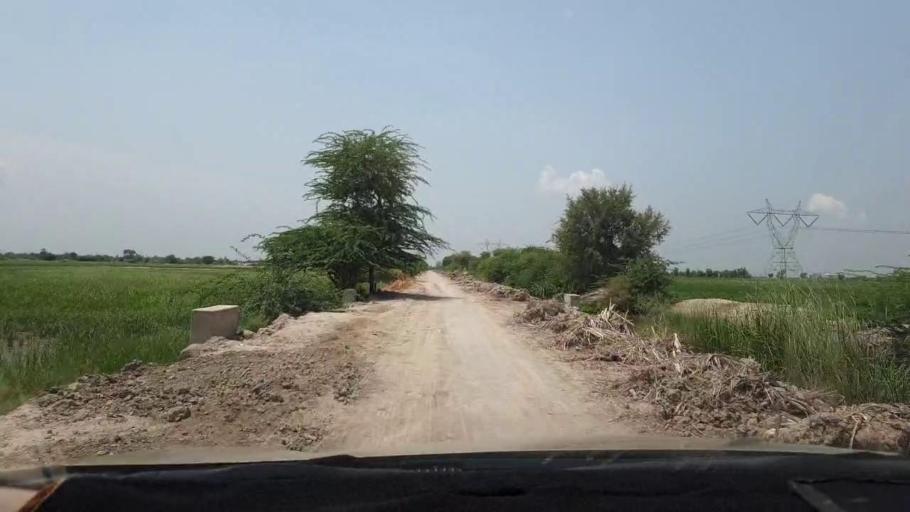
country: PK
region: Sindh
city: Naudero
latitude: 27.6676
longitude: 68.2848
